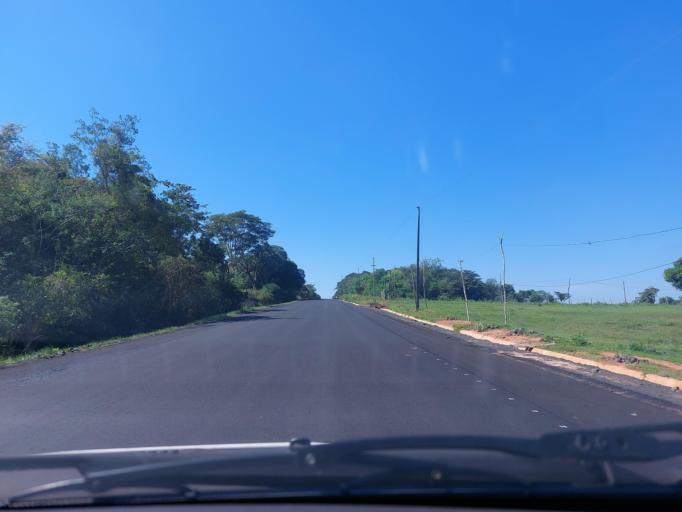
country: PY
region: San Pedro
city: Guayaybi
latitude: -24.5503
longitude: -56.5005
